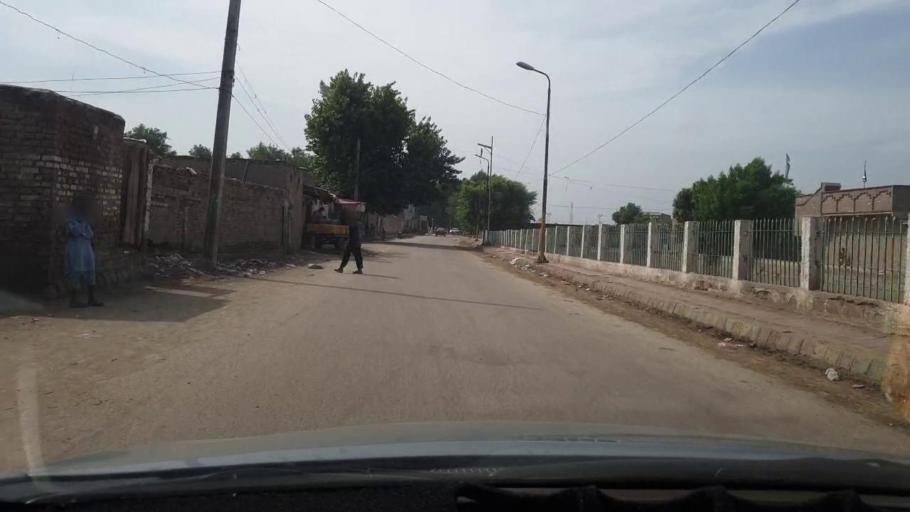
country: PK
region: Sindh
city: Khairpur
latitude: 27.5374
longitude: 68.7521
